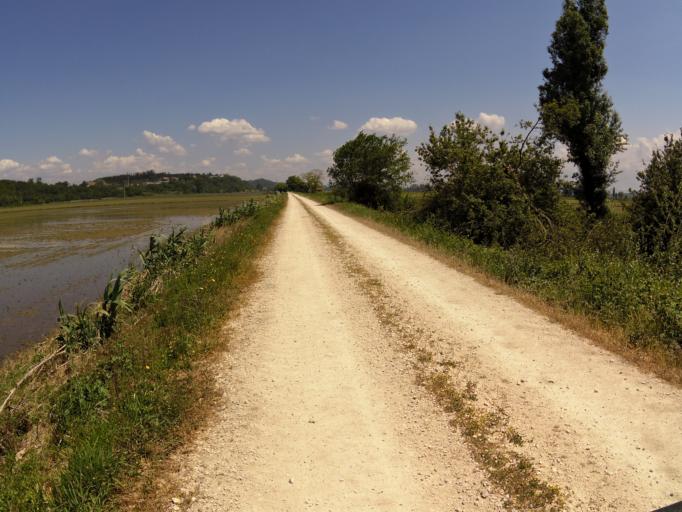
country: PT
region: Coimbra
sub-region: Montemor-O-Velho
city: Montemor-o-Velho
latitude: 40.1655
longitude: -8.7171
